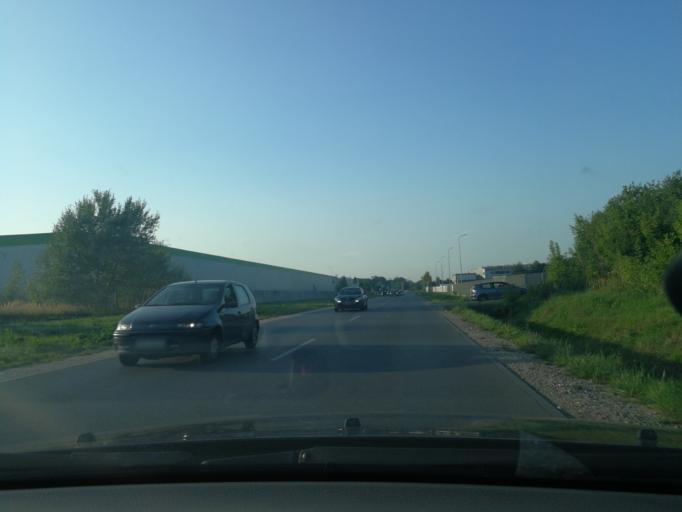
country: PL
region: Masovian Voivodeship
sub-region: Powiat pruszkowski
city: Brwinow
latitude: 52.1745
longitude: 20.7503
